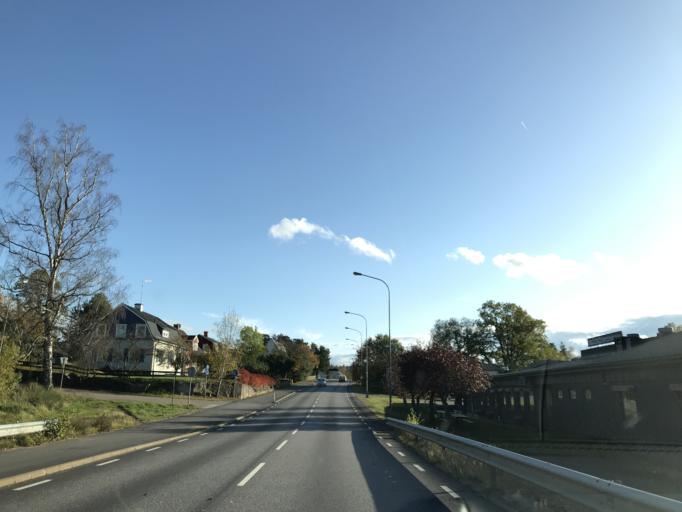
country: SE
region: Kalmar
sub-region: Hultsfreds Kommun
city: Virserum
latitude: 57.4107
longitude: 15.6186
